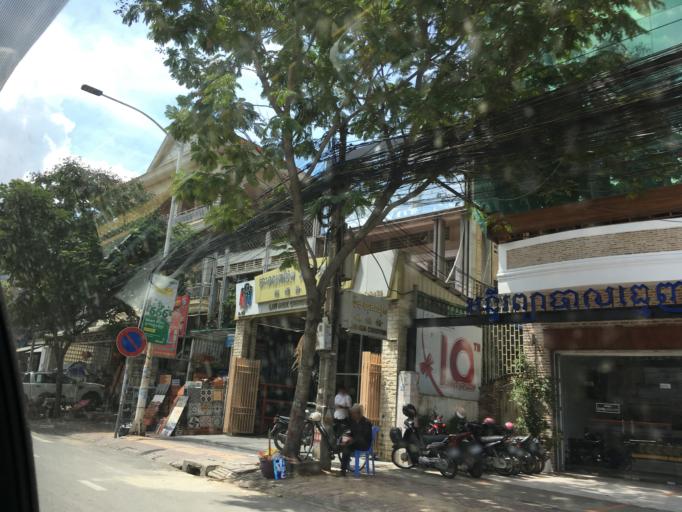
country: KH
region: Phnom Penh
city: Phnom Penh
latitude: 11.5439
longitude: 104.9131
